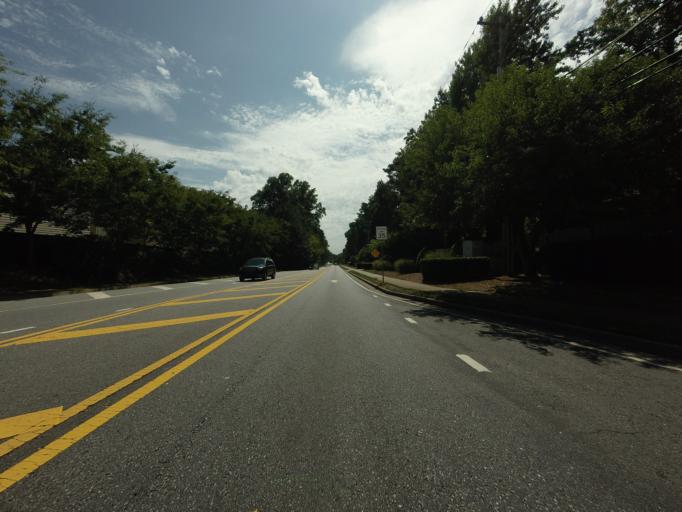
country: US
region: Georgia
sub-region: Fulton County
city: Johns Creek
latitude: 34.0689
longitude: -84.2034
